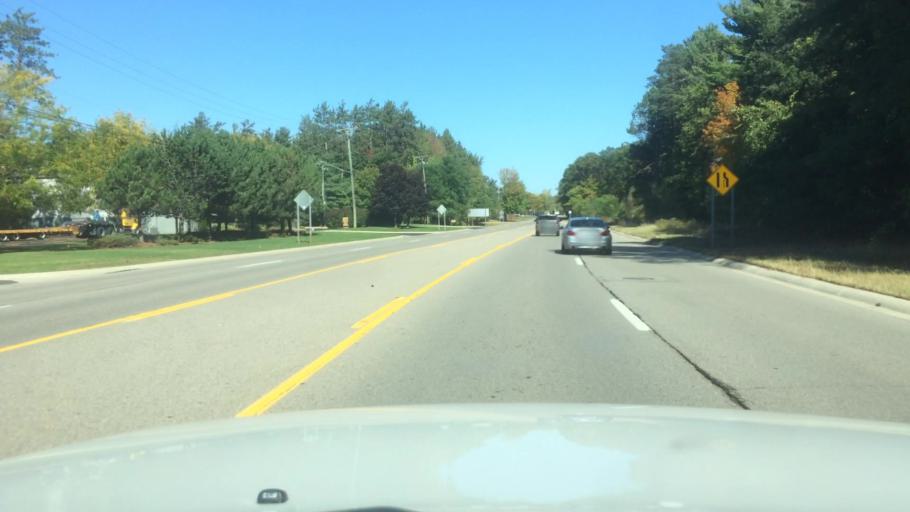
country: US
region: Michigan
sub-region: Oakland County
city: Wolverine Lake
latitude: 42.5714
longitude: -83.4498
